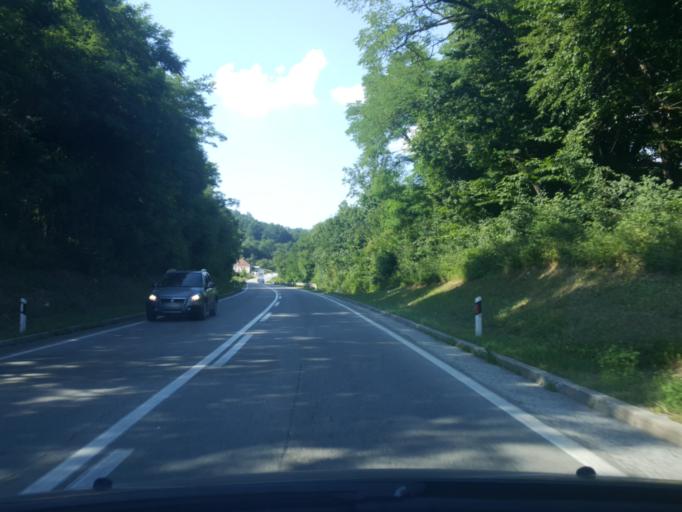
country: RS
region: Central Serbia
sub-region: Moravicki Okrug
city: Gornji Milanovac
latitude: 44.0966
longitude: 20.4814
